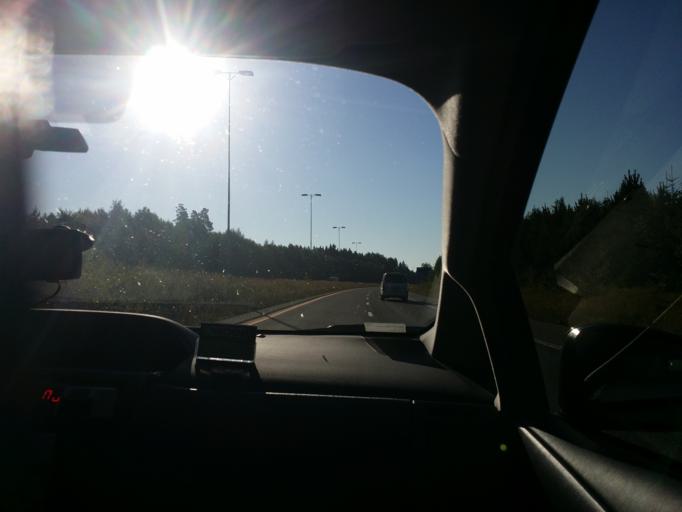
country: NO
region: Akershus
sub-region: Ullensaker
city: Jessheim
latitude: 60.1664
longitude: 11.1272
